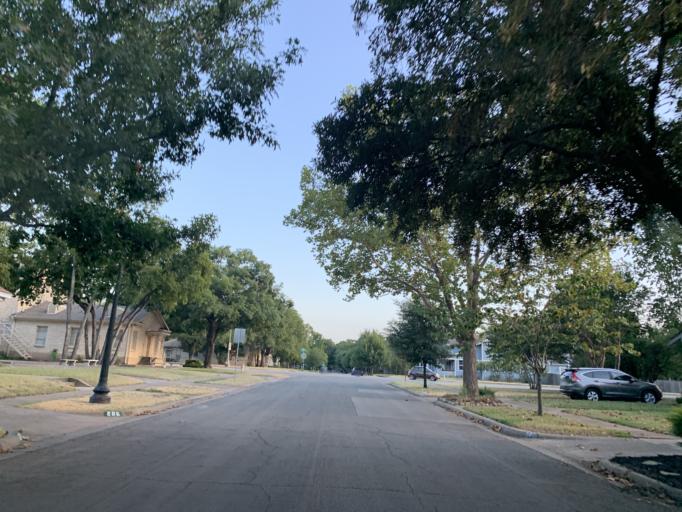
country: US
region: Texas
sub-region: Dallas County
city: Cockrell Hill
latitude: 32.7441
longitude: -96.8417
